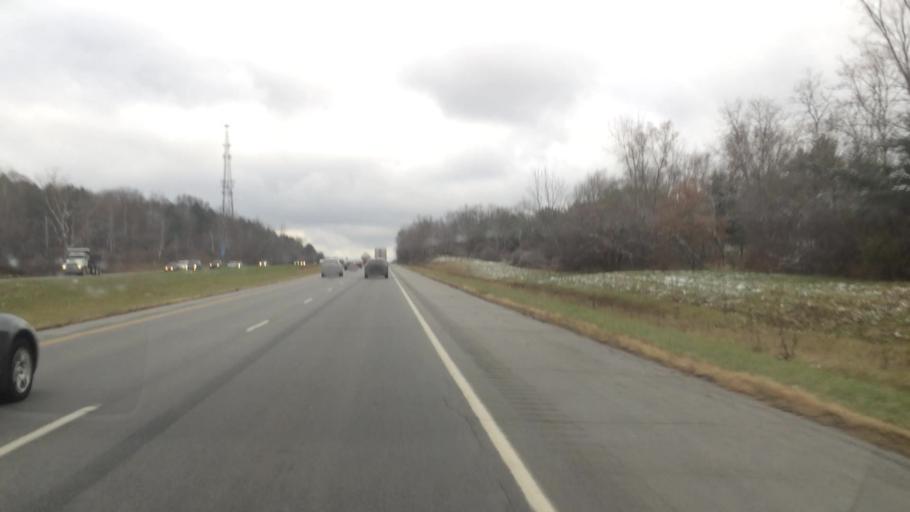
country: US
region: Ohio
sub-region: Summit County
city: Hudson
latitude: 41.2756
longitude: -81.4085
